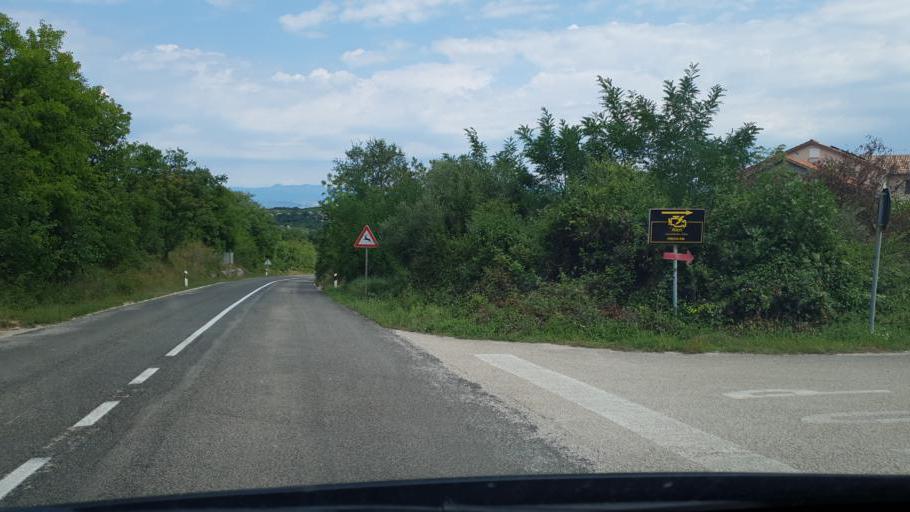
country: HR
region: Primorsko-Goranska
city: Njivice
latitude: 45.1368
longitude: 14.5836
